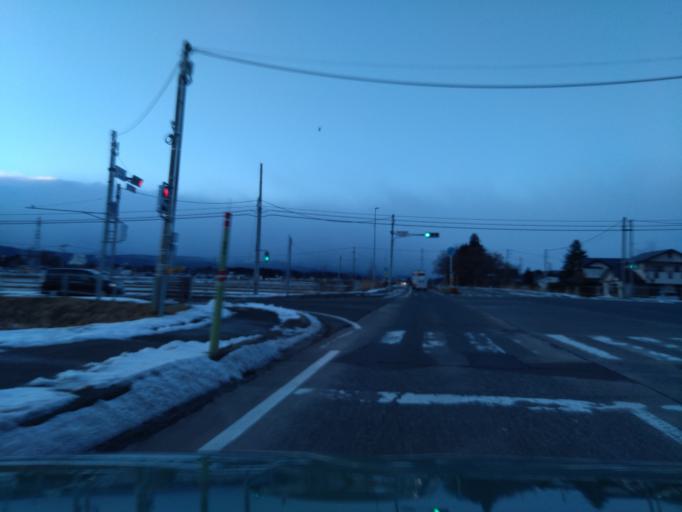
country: JP
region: Iwate
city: Shizukuishi
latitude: 39.6985
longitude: 140.9772
